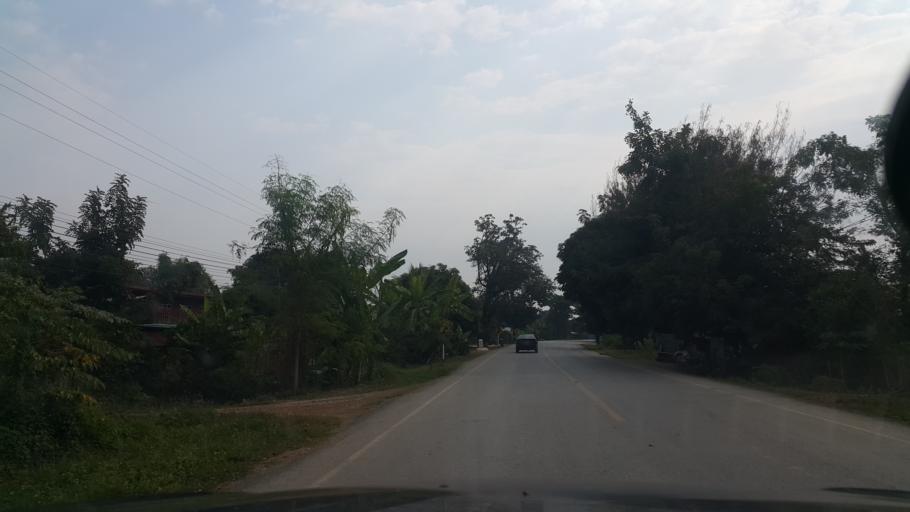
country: TH
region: Sukhothai
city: Si Samrong
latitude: 17.1829
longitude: 99.8306
